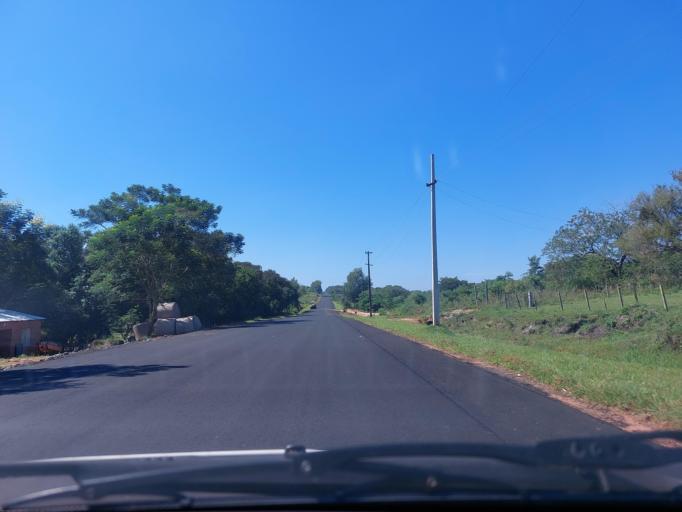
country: PY
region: San Pedro
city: Guayaybi
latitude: -24.5502
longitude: -56.5133
